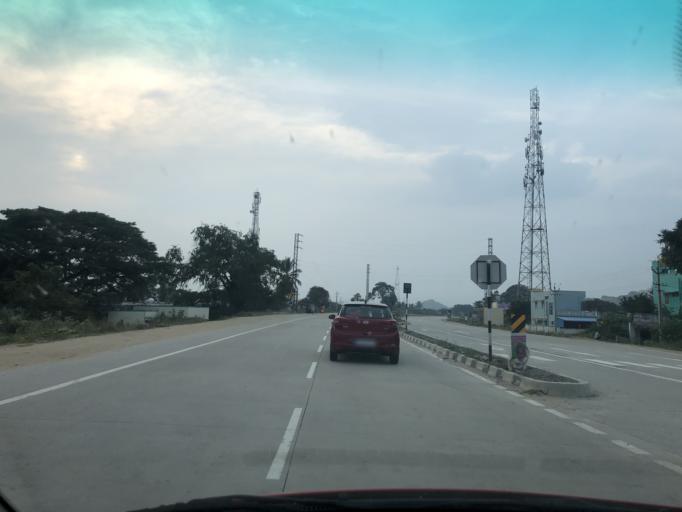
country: IN
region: Andhra Pradesh
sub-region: Chittoor
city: Chittoor
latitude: 13.1958
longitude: 79.0051
